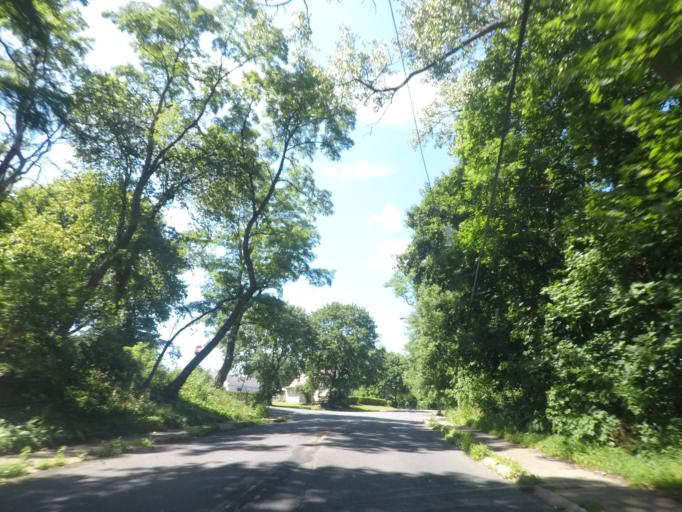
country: US
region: New York
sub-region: Schenectady County
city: Rotterdam
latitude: 42.7948
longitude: -73.9578
